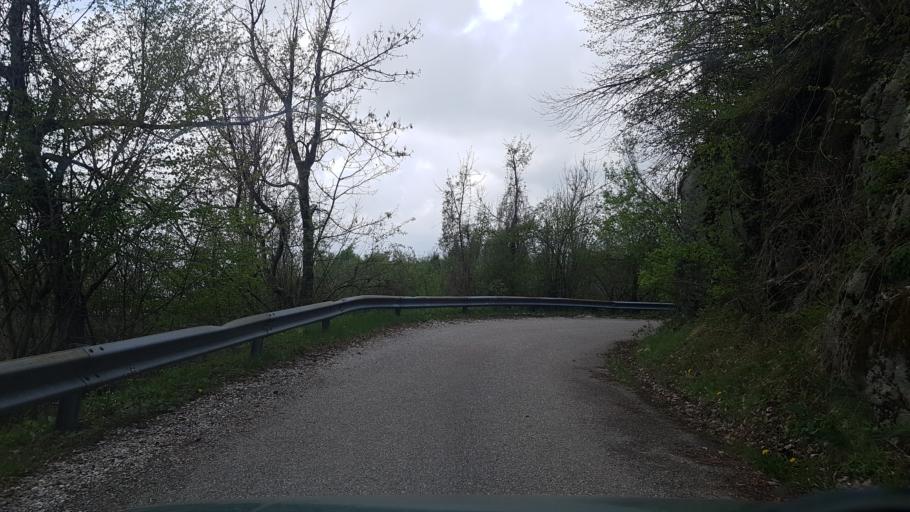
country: IT
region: Friuli Venezia Giulia
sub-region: Provincia di Udine
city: Faedis
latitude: 46.1902
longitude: 13.3619
